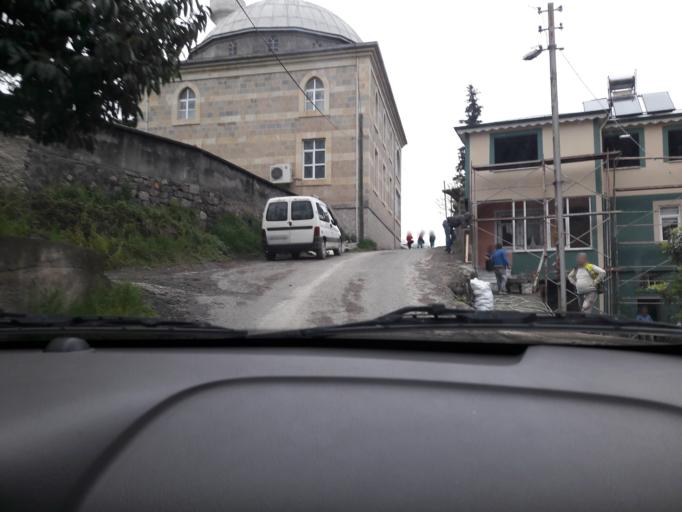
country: TR
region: Trabzon
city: Duzkoy
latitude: 40.9139
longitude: 39.4824
